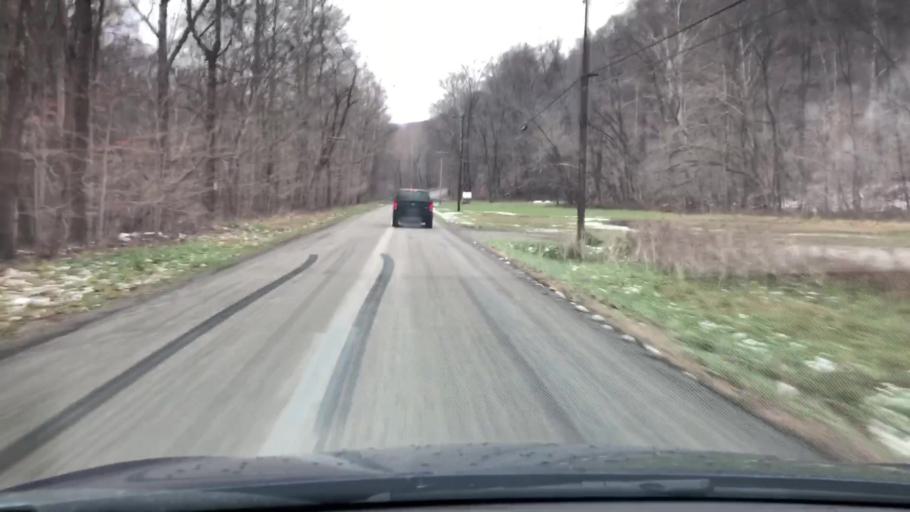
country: US
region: Pennsylvania
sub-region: Fayette County
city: Dunbar
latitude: 39.9646
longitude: -79.5867
